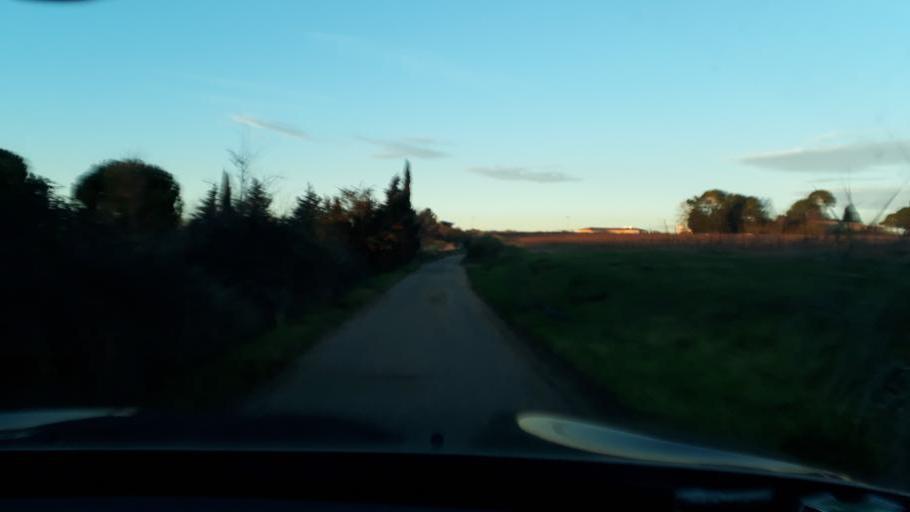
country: FR
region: Languedoc-Roussillon
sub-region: Departement de l'Herault
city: Florensac
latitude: 43.3941
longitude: 3.4593
